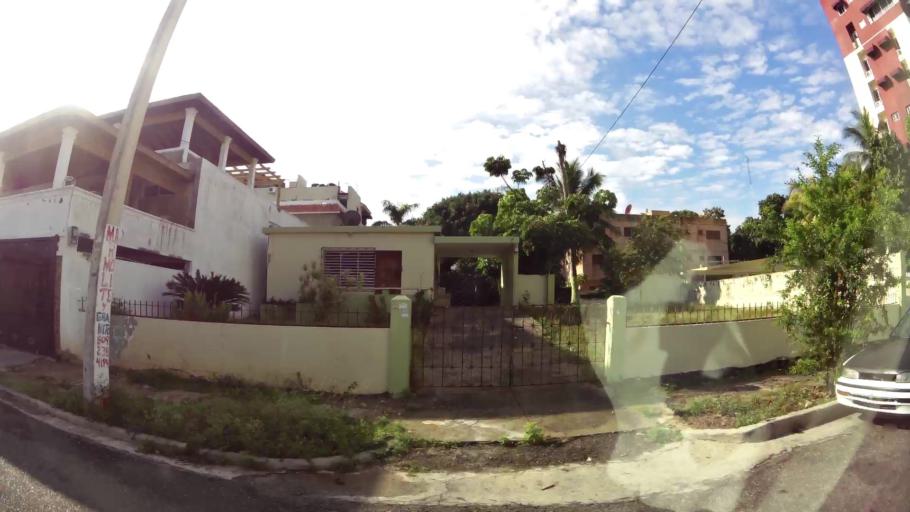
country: DO
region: Santo Domingo
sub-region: Santo Domingo
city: Santo Domingo Este
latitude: 18.4879
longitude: -69.8582
